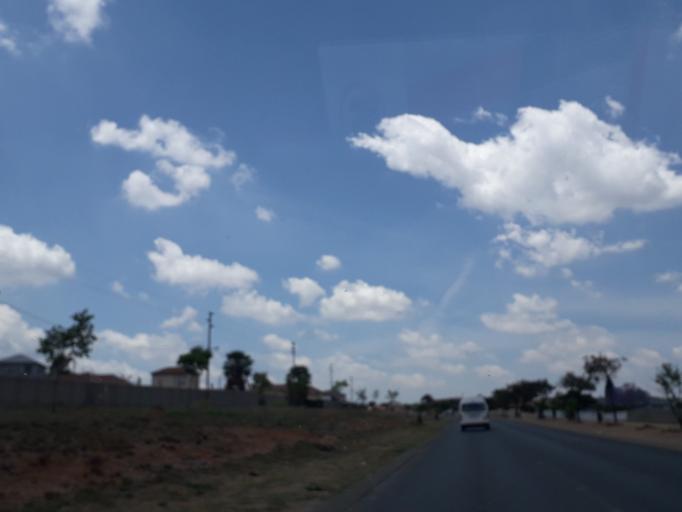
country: ZA
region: Gauteng
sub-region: West Rand District Municipality
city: Muldersdriseloop
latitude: -26.0439
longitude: 27.9222
